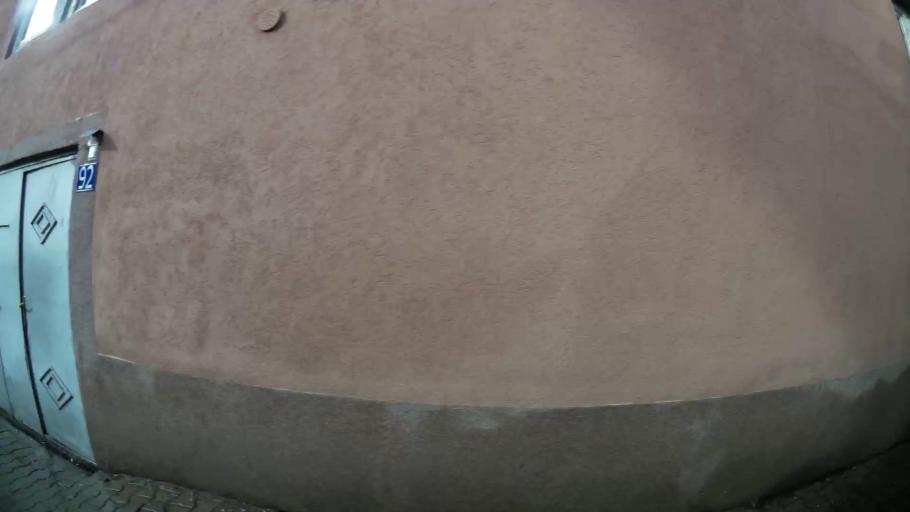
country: XK
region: Pristina
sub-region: Komuna e Prishtines
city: Pristina
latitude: 42.6800
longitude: 21.1762
